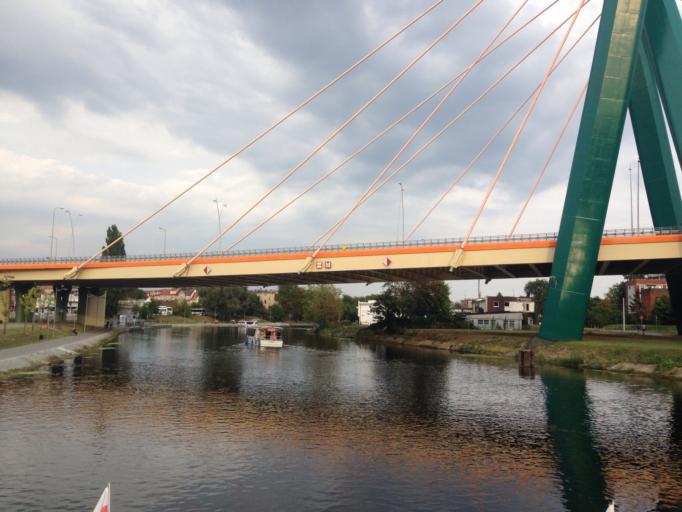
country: PL
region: Kujawsko-Pomorskie
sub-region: Bydgoszcz
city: Bydgoszcz
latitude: 53.1209
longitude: 18.0160
